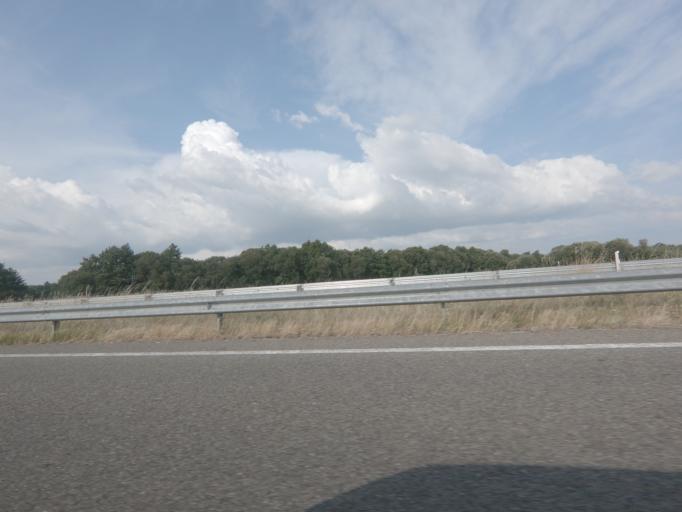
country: ES
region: Galicia
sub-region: Provincia de Ourense
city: Xinzo de Limia
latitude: 42.1315
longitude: -7.7420
